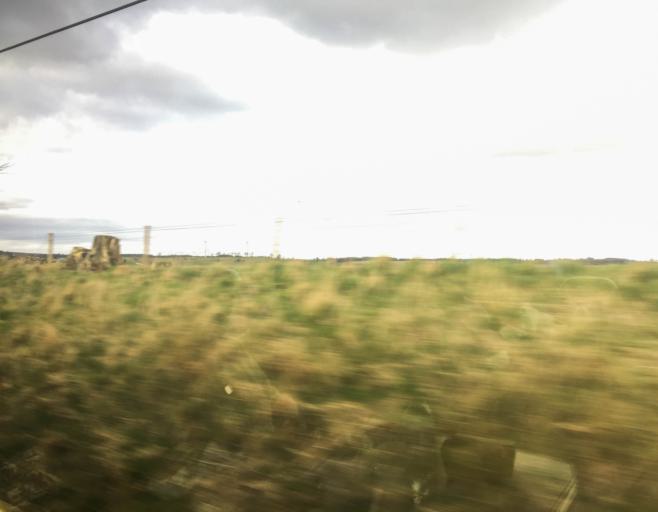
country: GB
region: Scotland
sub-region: South Lanarkshire
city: Carnwath
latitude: 55.6759
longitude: -3.6466
